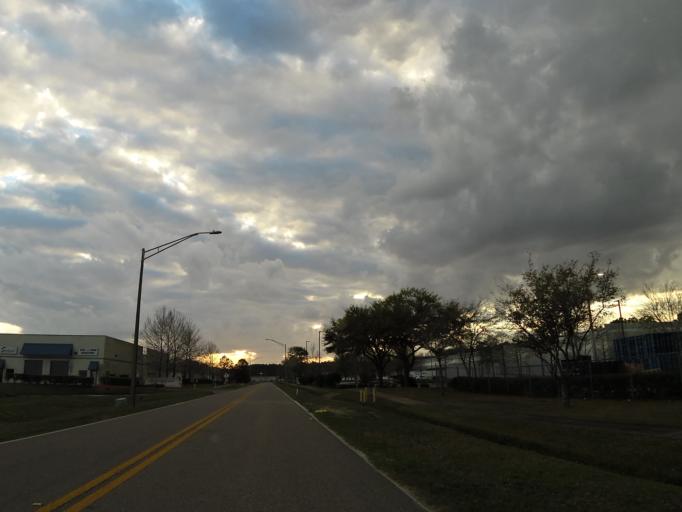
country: US
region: Florida
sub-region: Saint Johns County
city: Fruit Cove
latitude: 30.1867
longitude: -81.5681
